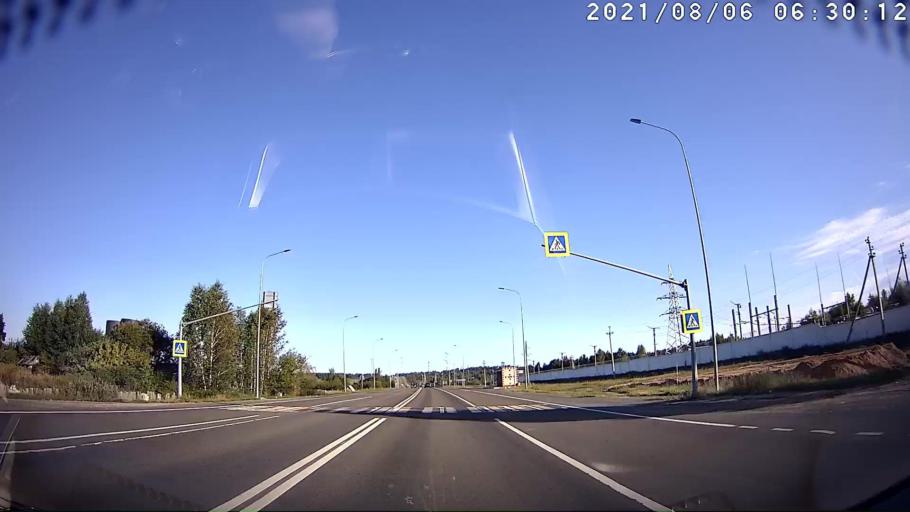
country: RU
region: Mariy-El
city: Krasnogorskiy
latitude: 56.1635
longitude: 48.2886
